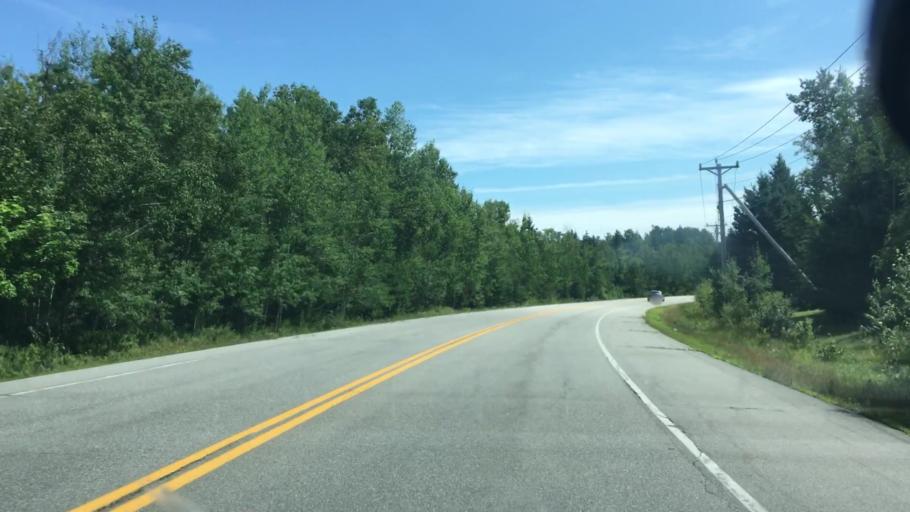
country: US
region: Maine
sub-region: Washington County
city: Eastport
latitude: 44.9364
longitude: -67.0268
